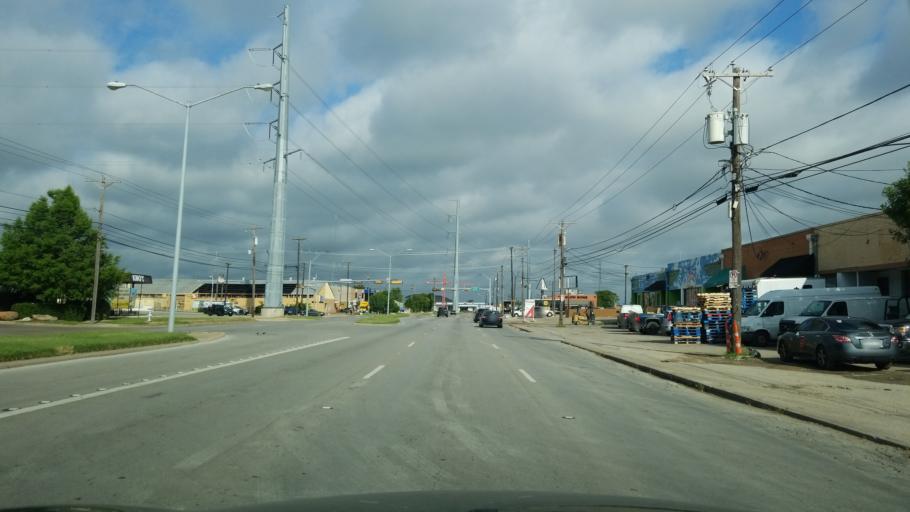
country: US
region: Texas
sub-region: Dallas County
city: Dallas
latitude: 32.7958
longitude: -96.8323
